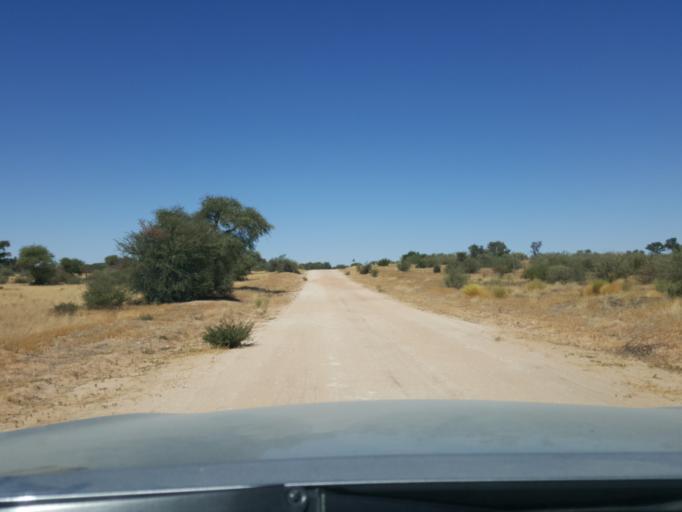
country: BW
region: Kgalagadi
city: Hukuntsi
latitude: -23.9799
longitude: 21.2078
